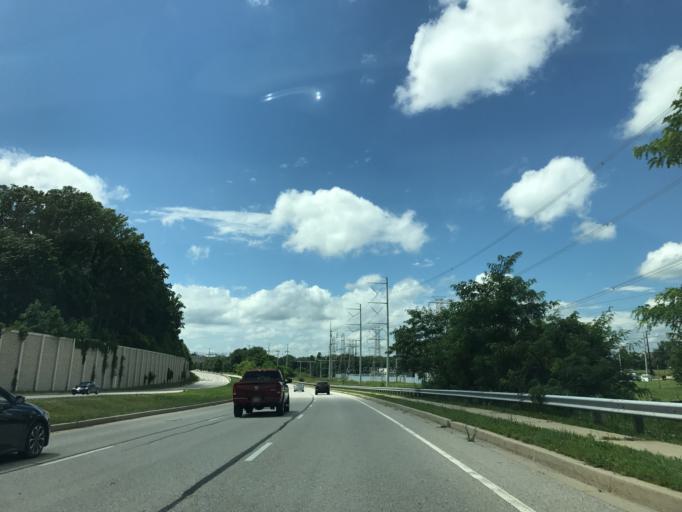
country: US
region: Maryland
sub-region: Howard County
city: North Laurel
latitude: 39.1369
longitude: -76.8696
